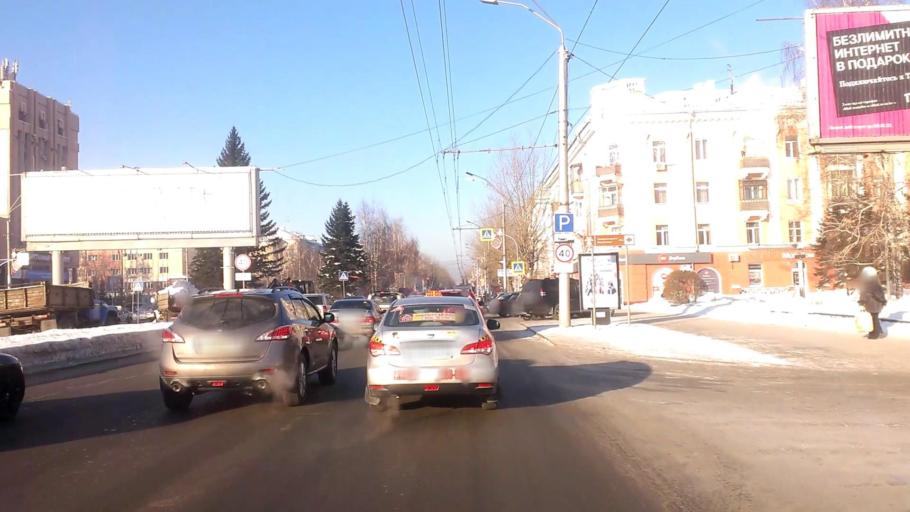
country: RU
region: Altai Krai
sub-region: Gorod Barnaulskiy
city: Barnaul
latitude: 53.3475
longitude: 83.7779
